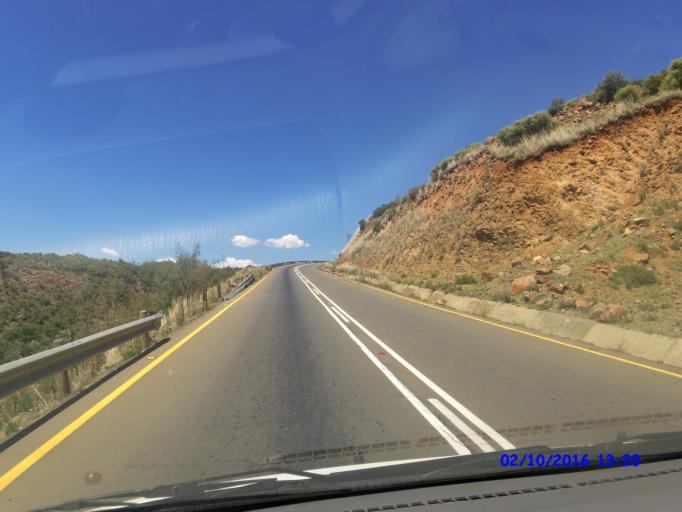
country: LS
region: Maseru
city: Nako
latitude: -29.4216
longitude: 27.7038
